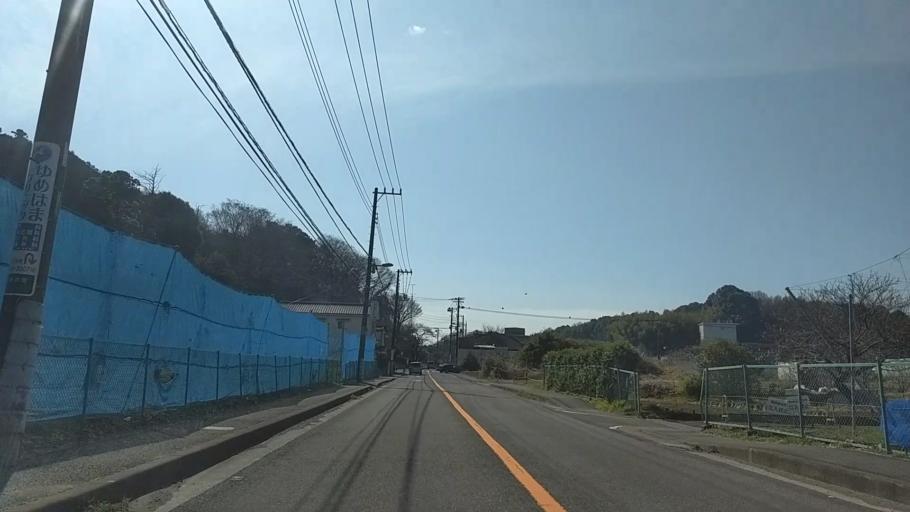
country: JP
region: Kanagawa
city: Kamakura
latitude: 35.4051
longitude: 139.5532
